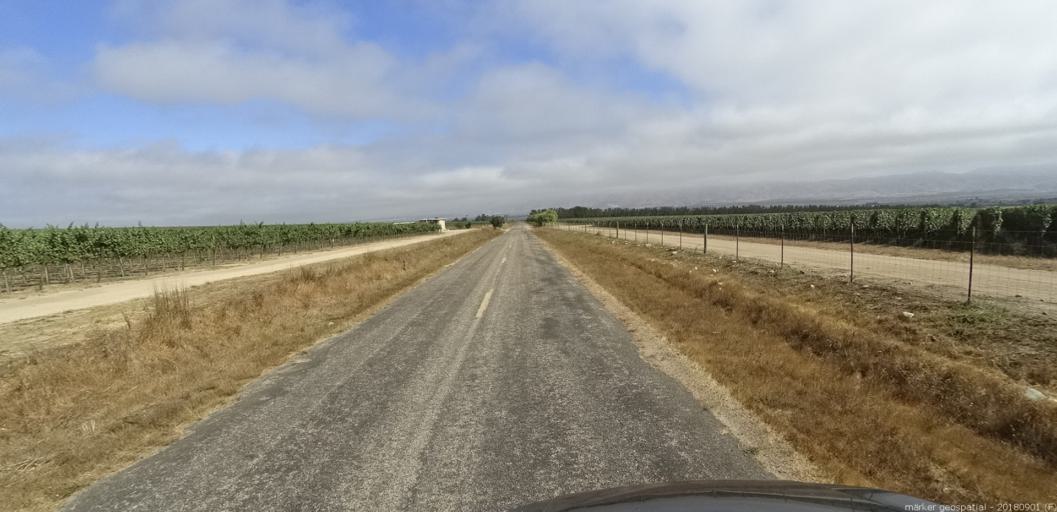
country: US
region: California
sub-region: Monterey County
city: Soledad
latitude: 36.3578
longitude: -121.3355
